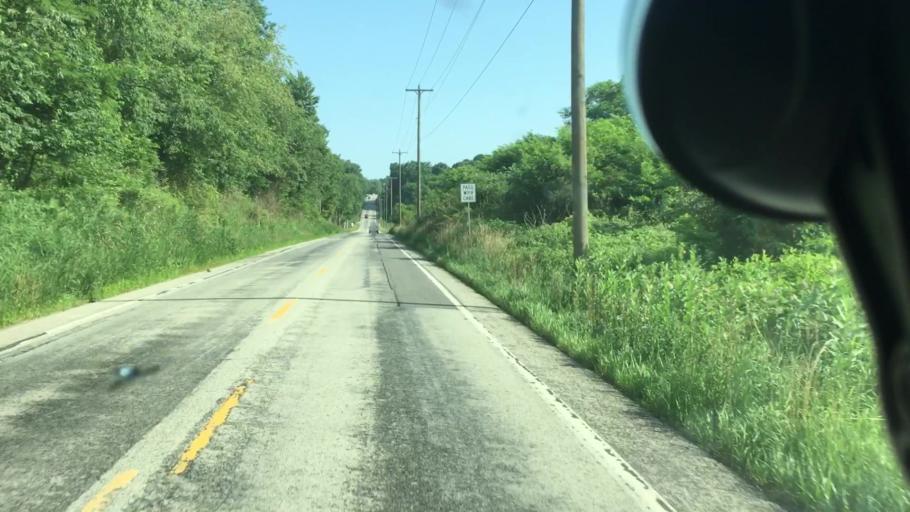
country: US
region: Pennsylvania
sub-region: Lawrence County
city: New Castle
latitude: 40.9934
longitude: -80.2684
